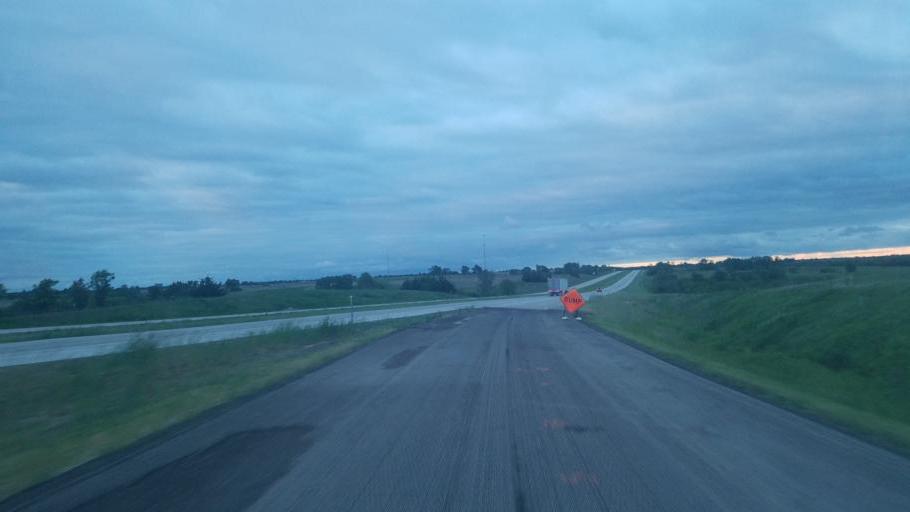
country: US
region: Iowa
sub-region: Decatur County
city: Lamoni
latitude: 40.5776
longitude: -93.9344
